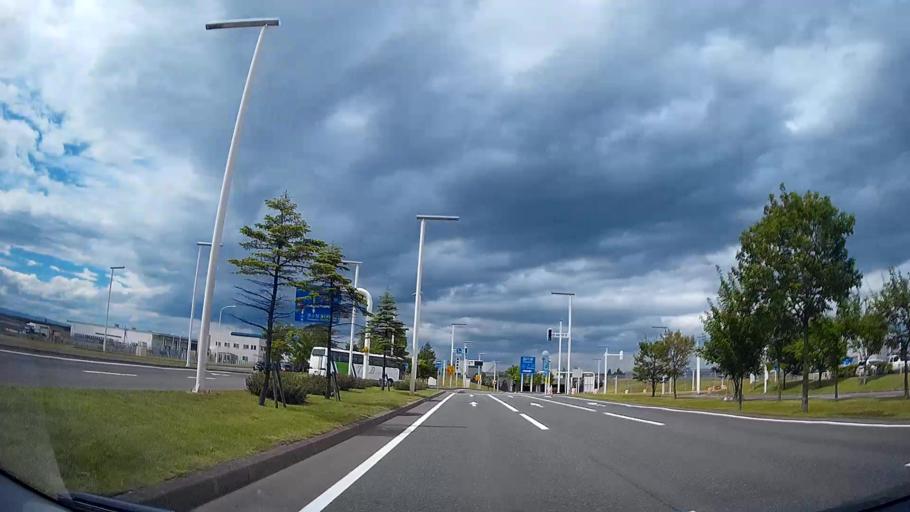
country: JP
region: Hokkaido
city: Chitose
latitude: 42.7883
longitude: 141.6765
